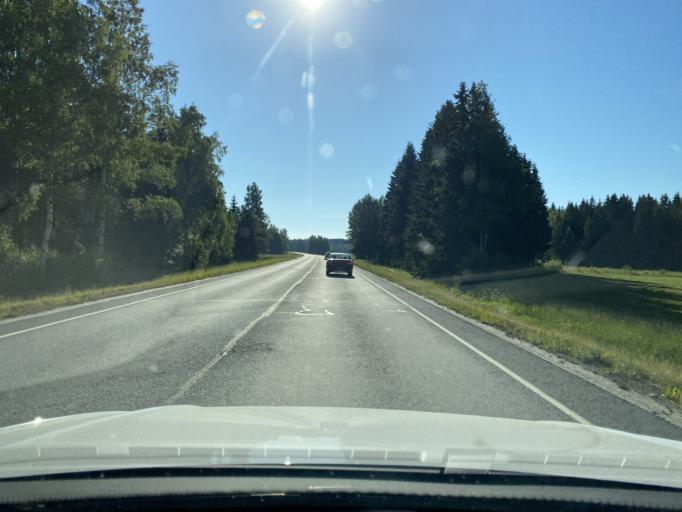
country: FI
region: Haeme
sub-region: Forssa
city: Tammela
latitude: 60.8257
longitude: 23.7845
